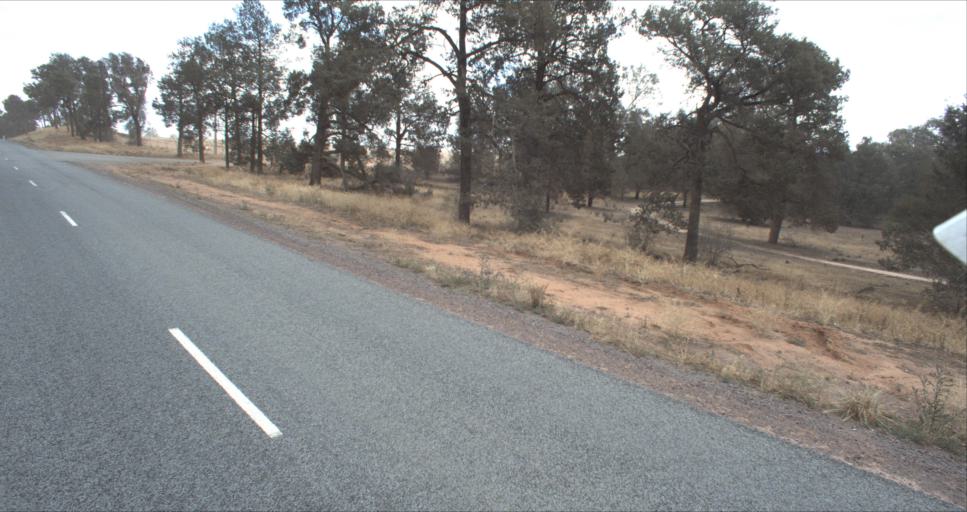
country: AU
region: New South Wales
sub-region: Leeton
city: Leeton
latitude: -34.6576
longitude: 146.3500
